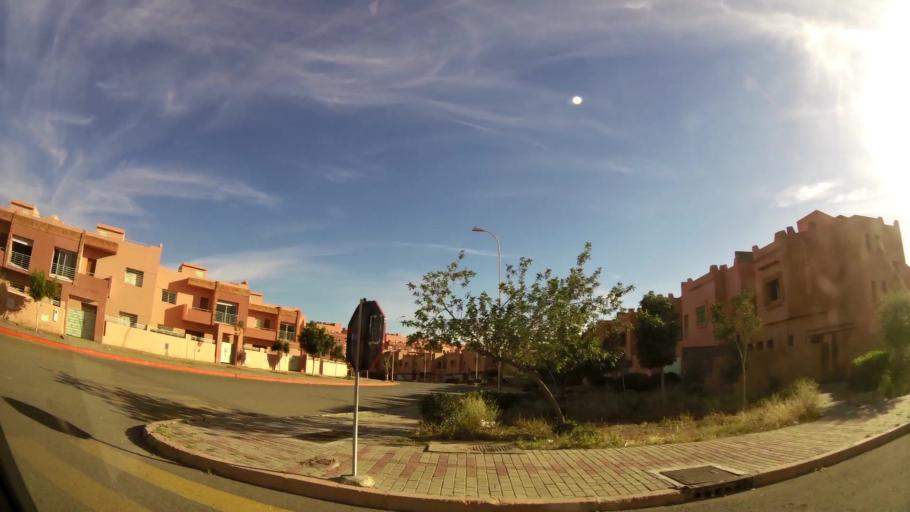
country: MA
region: Marrakech-Tensift-Al Haouz
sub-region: Marrakech
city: Marrakesh
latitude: 31.7510
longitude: -8.1060
